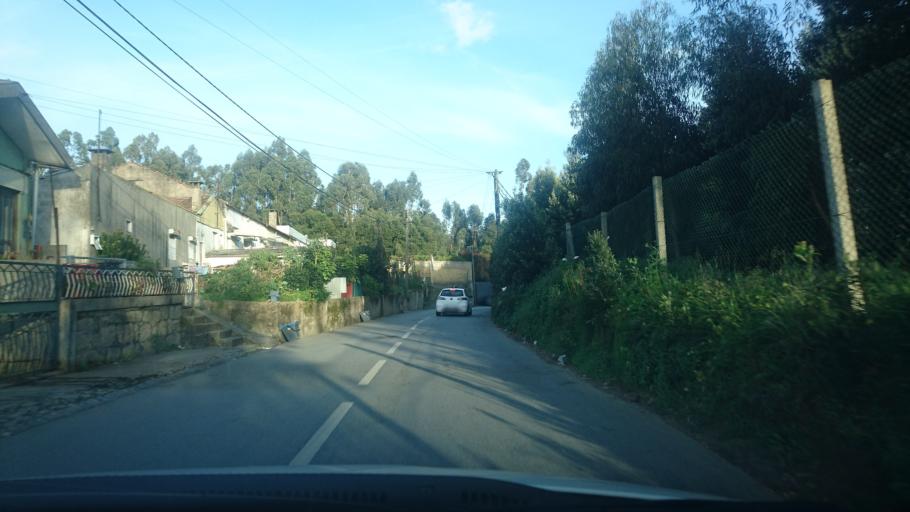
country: PT
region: Aveiro
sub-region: Santa Maria da Feira
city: Nogueira da Regedoura
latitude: 41.0004
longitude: -8.6038
